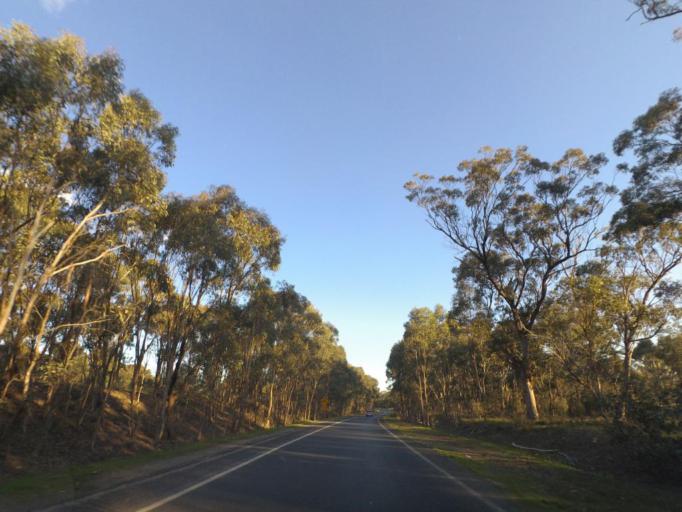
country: AU
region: Victoria
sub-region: Murrindindi
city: Kinglake West
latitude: -37.0652
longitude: 145.1020
